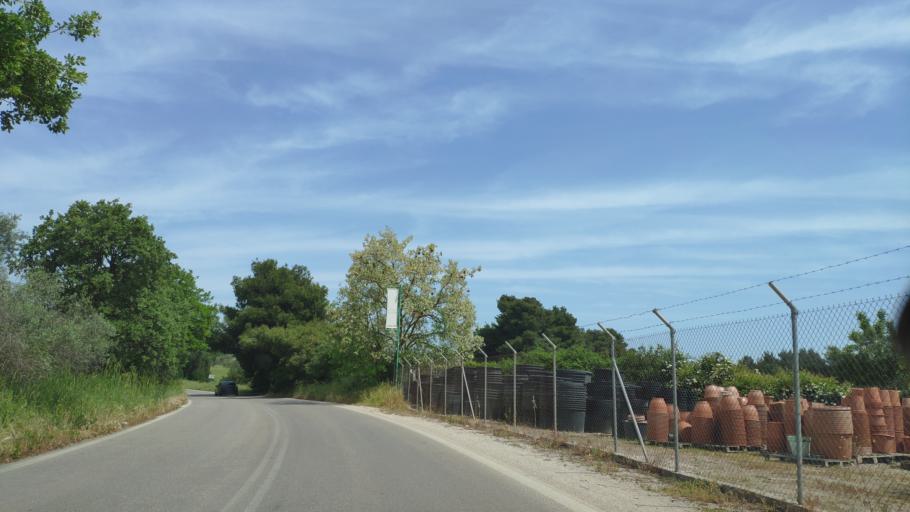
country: GR
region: Attica
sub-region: Nomarchia Anatolikis Attikis
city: Agios Stefanos
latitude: 38.1711
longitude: 23.8619
